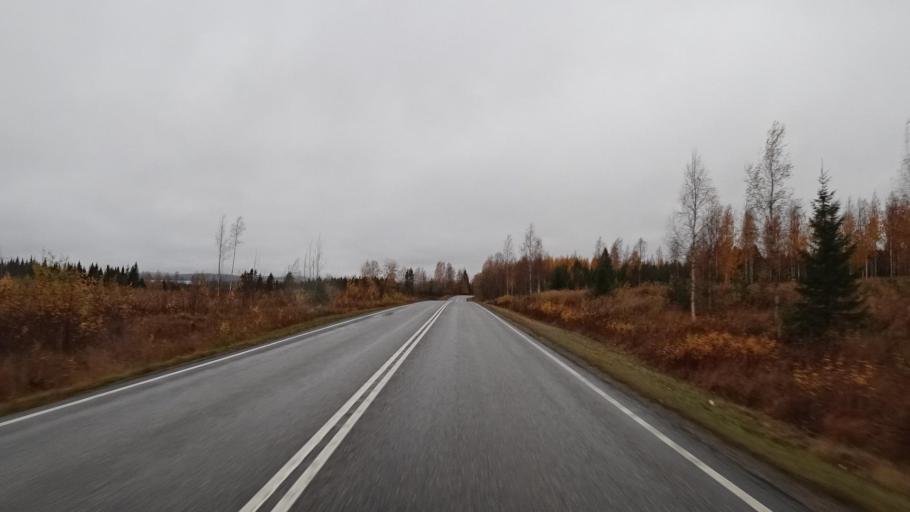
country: FI
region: Northern Savo
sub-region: Koillis-Savo
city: Tuusniemi
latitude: 62.7896
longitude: 28.5807
